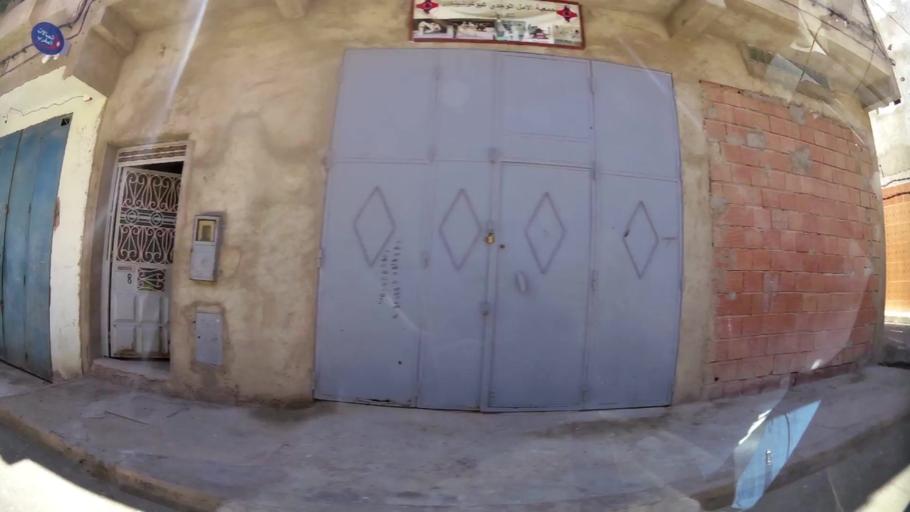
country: MA
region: Oriental
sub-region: Oujda-Angad
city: Oujda
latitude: 34.6884
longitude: -1.9517
